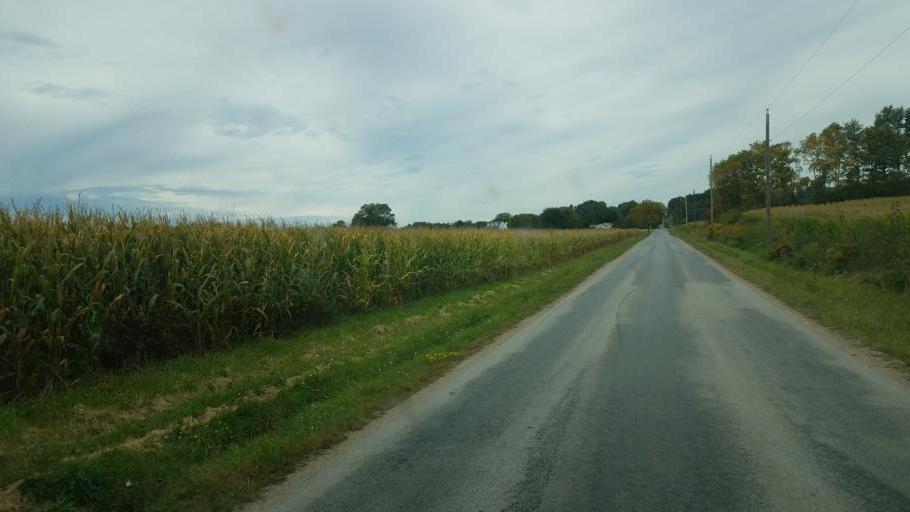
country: US
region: Ohio
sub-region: Knox County
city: Centerburg
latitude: 40.3209
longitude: -82.7130
